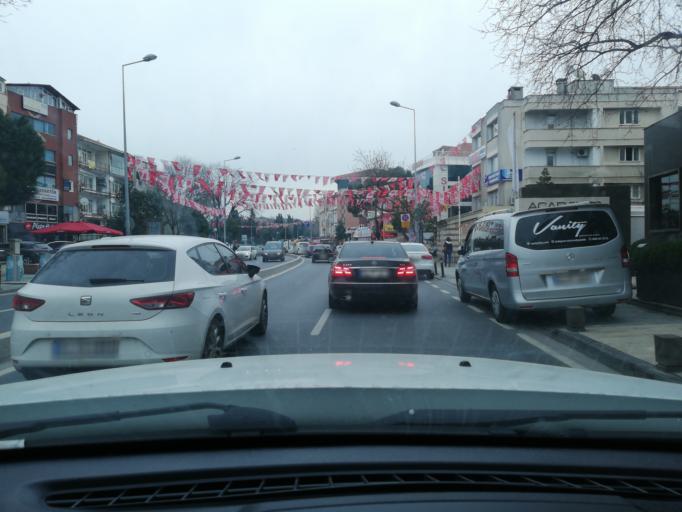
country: TR
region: Istanbul
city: UEskuedar
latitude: 41.0200
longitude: 29.0345
